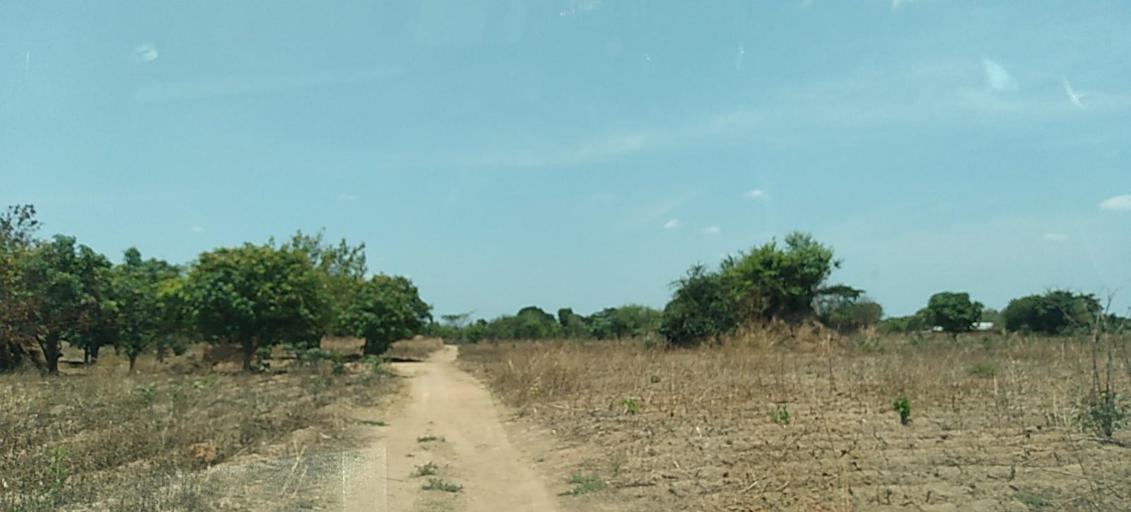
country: ZM
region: Copperbelt
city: Luanshya
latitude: -13.0612
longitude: 28.4095
